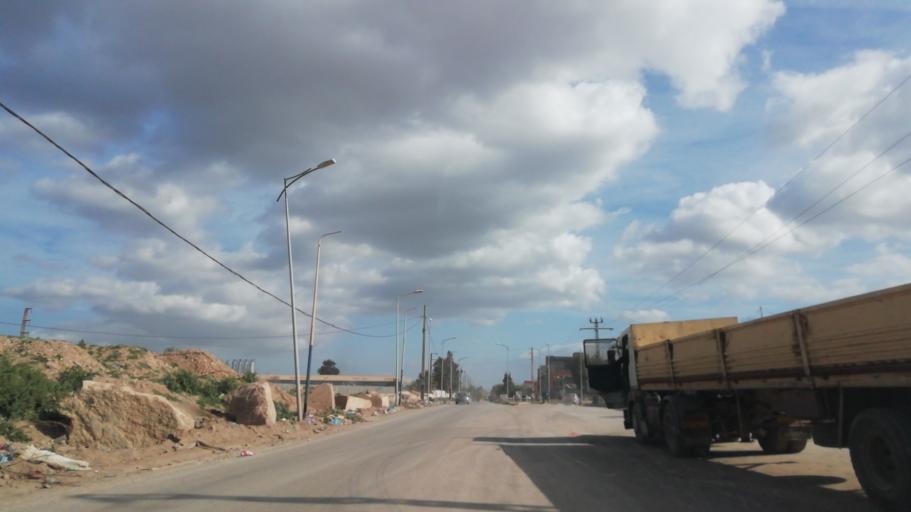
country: DZ
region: Oran
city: Es Senia
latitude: 35.6516
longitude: -0.5810
